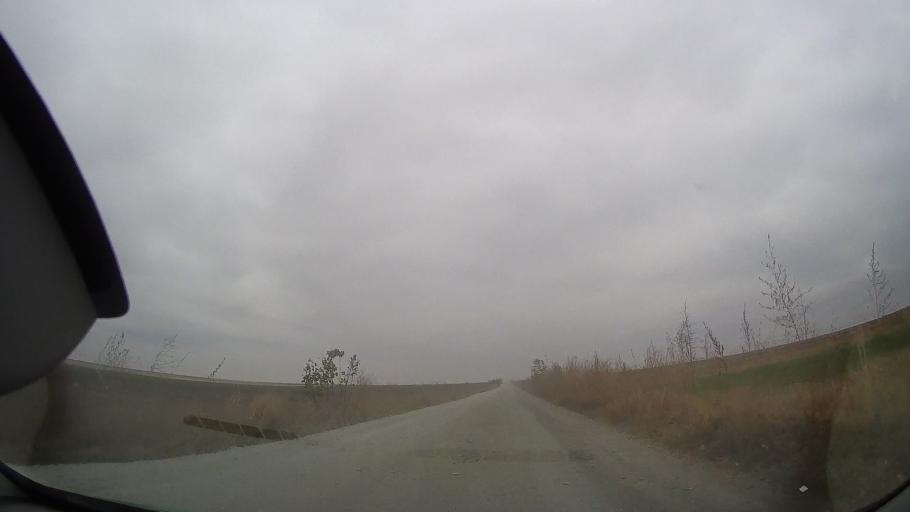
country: RO
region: Ialomita
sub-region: Comuna Grivita
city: Grivita
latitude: 44.7476
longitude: 27.2673
